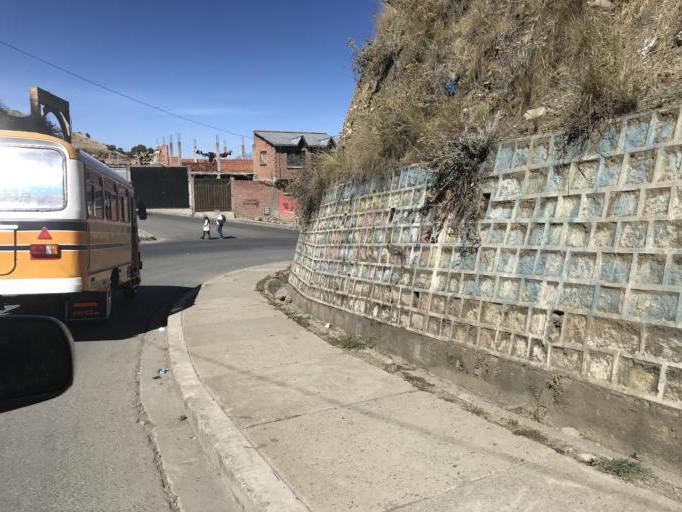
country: BO
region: La Paz
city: La Paz
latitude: -16.4844
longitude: -68.1682
